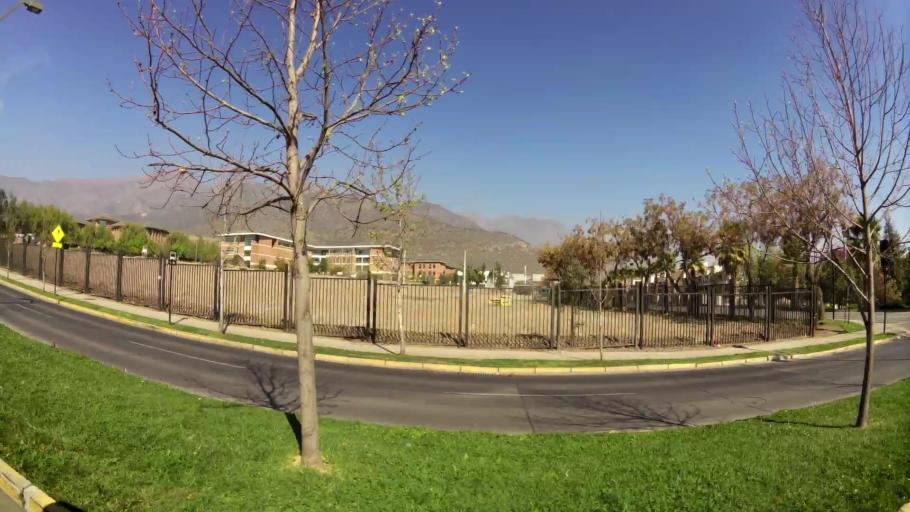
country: CL
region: Santiago Metropolitan
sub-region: Provincia de Santiago
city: Villa Presidente Frei, Nunoa, Santiago, Chile
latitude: -33.4014
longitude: -70.5096
